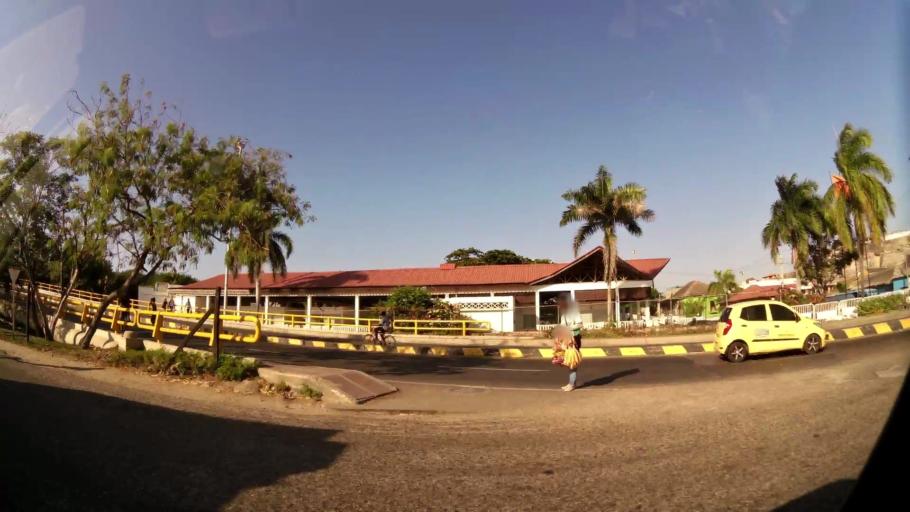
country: CO
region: Bolivar
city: Cartagena
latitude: 10.4222
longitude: -75.5416
